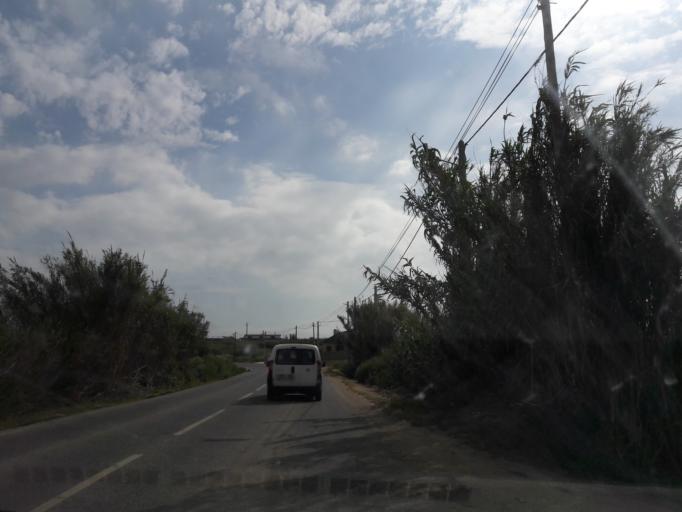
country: PT
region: Leiria
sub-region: Peniche
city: Atouguia da Baleia
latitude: 39.3456
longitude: -9.3264
